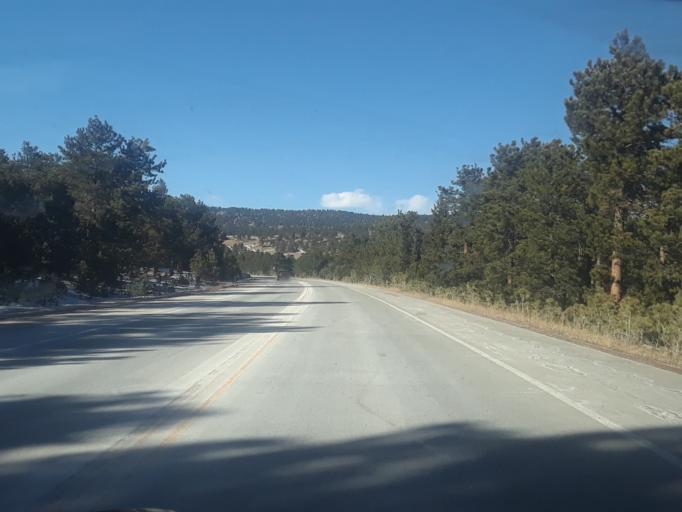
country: US
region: Colorado
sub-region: Boulder County
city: Lyons
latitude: 40.1784
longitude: -105.4711
